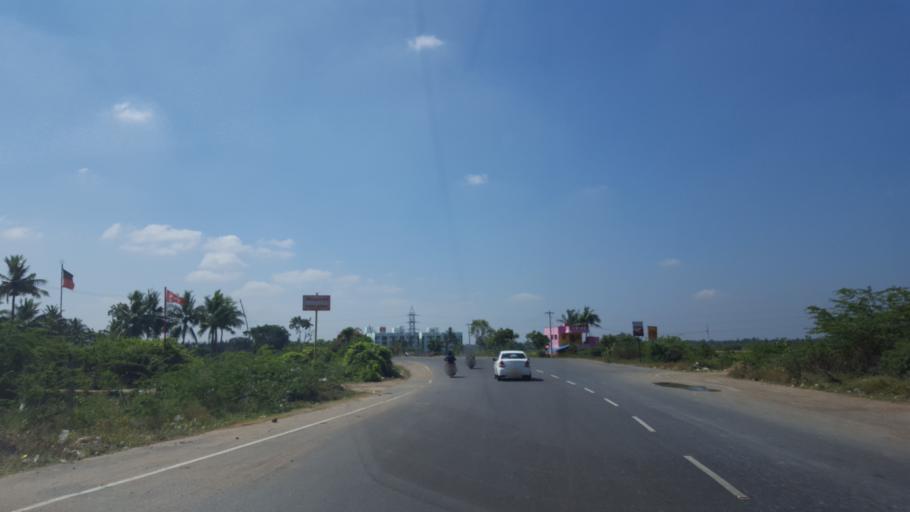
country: IN
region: Tamil Nadu
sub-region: Kancheepuram
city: Mamallapuram
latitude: 12.7127
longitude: 80.1869
